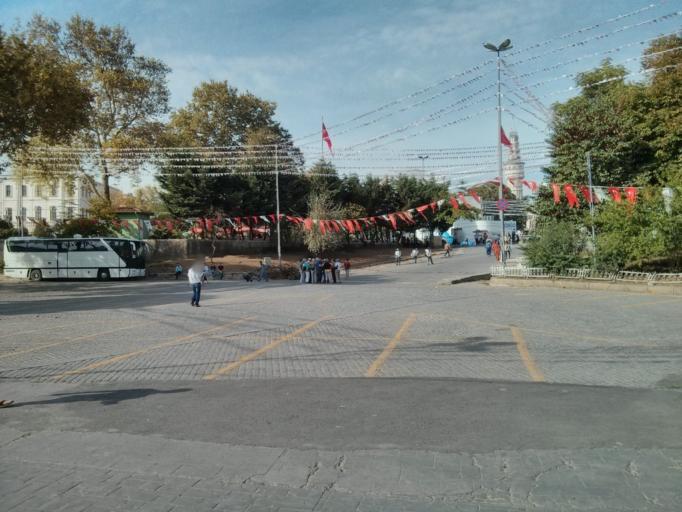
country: TR
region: Istanbul
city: Eminoenue
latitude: 41.0108
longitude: 28.9648
